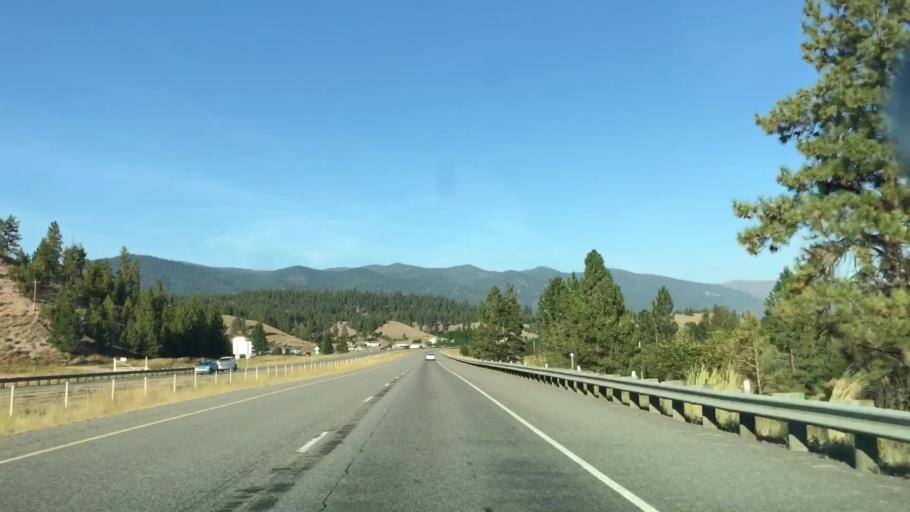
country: US
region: Montana
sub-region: Missoula County
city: Frenchtown
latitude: 47.0319
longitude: -114.3489
